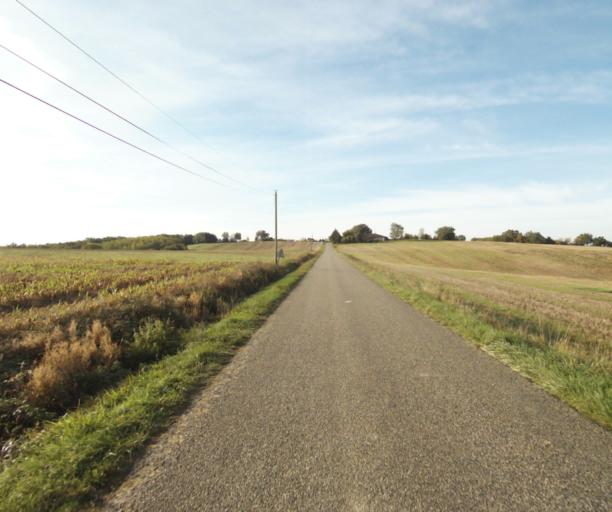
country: FR
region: Midi-Pyrenees
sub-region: Departement de la Haute-Garonne
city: Villemur-sur-Tarn
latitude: 43.9125
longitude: 1.4935
